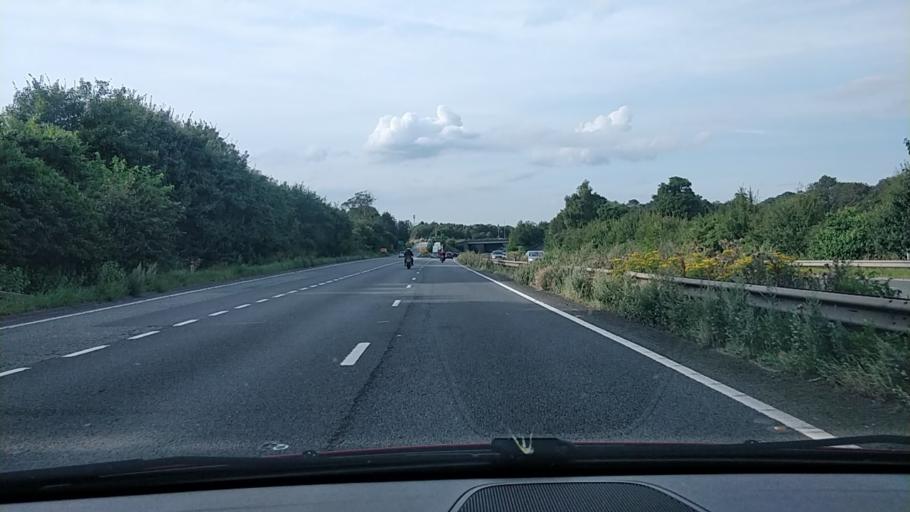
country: GB
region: England
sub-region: Cheshire West and Chester
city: Guilden Sutton
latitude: 53.1909
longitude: -2.8440
